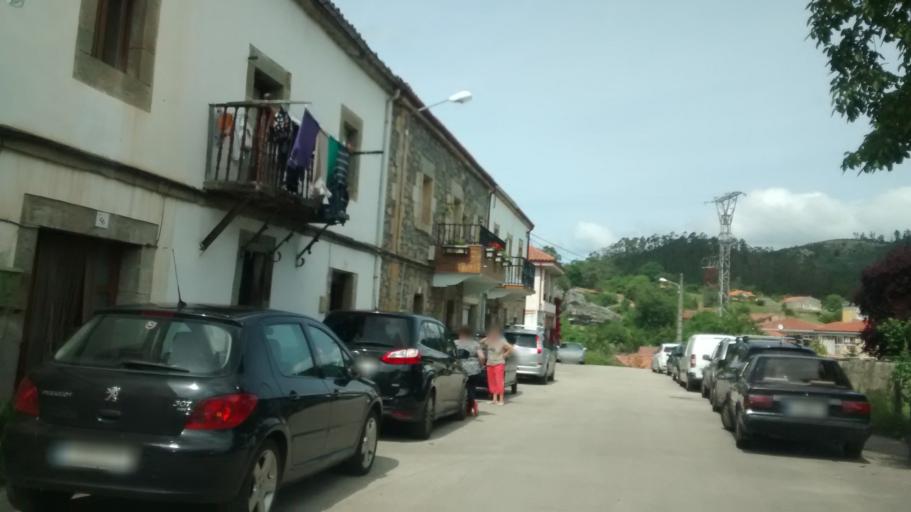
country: ES
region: Cantabria
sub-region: Provincia de Cantabria
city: Lierganes
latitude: 43.3521
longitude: -3.7099
